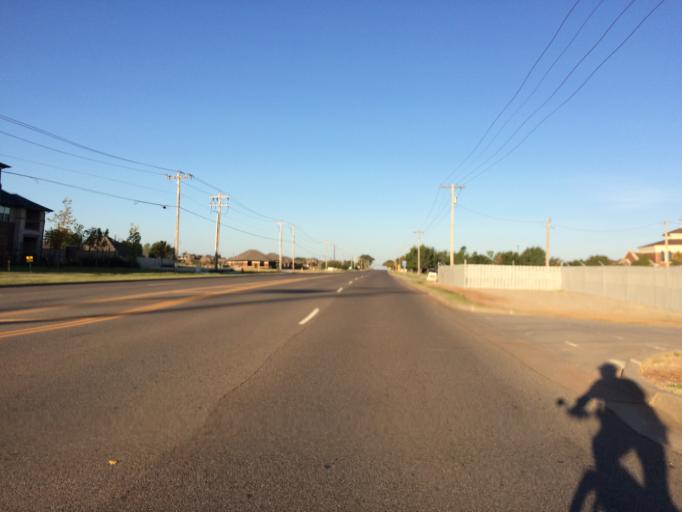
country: US
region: Oklahoma
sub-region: Cleveland County
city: Norman
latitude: 35.2620
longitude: -97.4955
